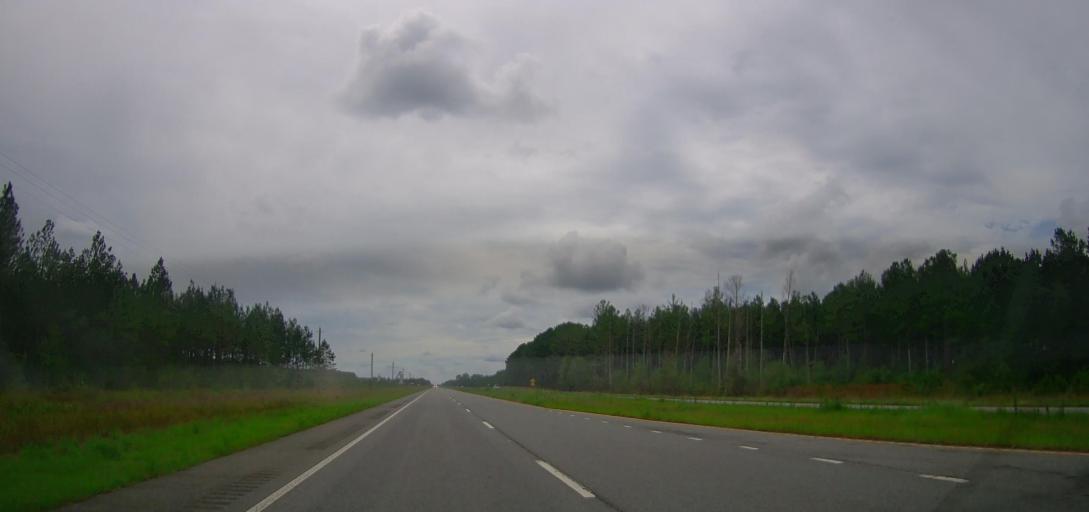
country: US
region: Georgia
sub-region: Appling County
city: Baxley
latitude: 31.7333
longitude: -82.2193
